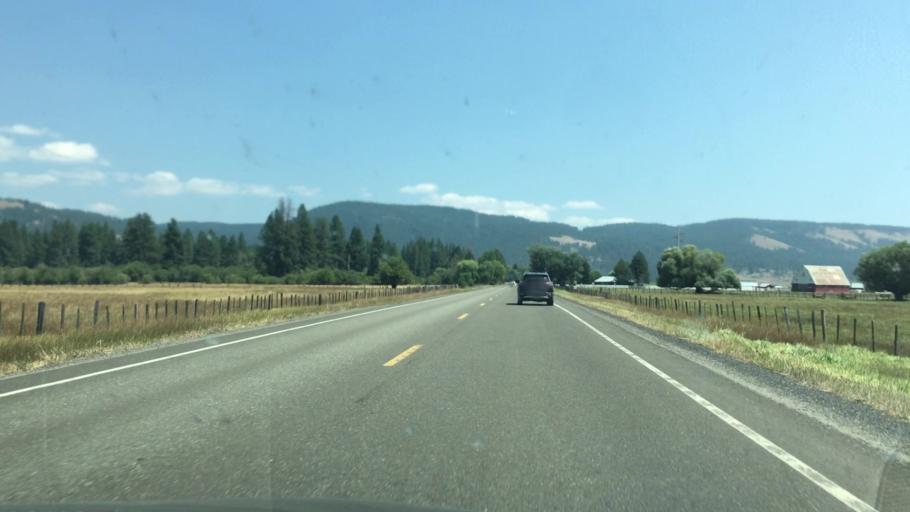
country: US
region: Idaho
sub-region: Valley County
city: McCall
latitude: 44.9645
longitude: -116.2599
